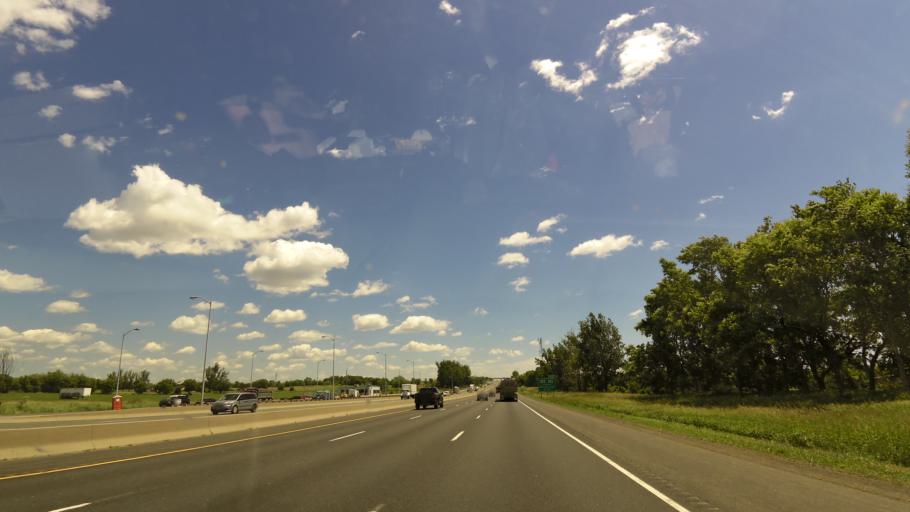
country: CA
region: Ontario
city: Oshawa
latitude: 43.9002
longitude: -78.6611
